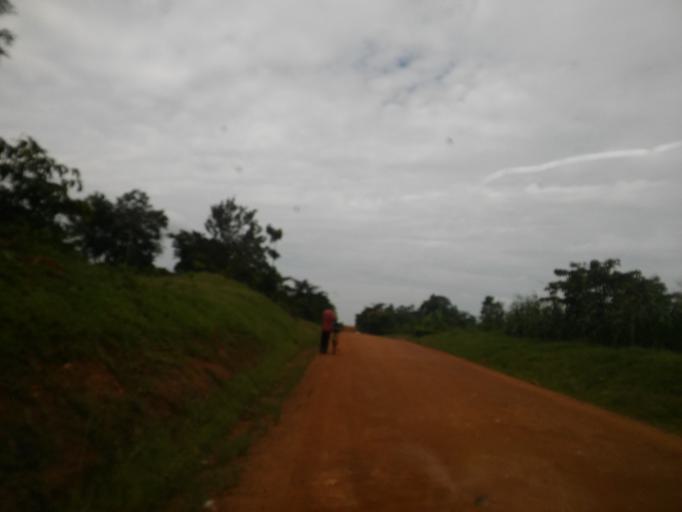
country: UG
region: Eastern Region
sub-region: Mbale District
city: Mbale
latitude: 0.9713
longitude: 34.2074
